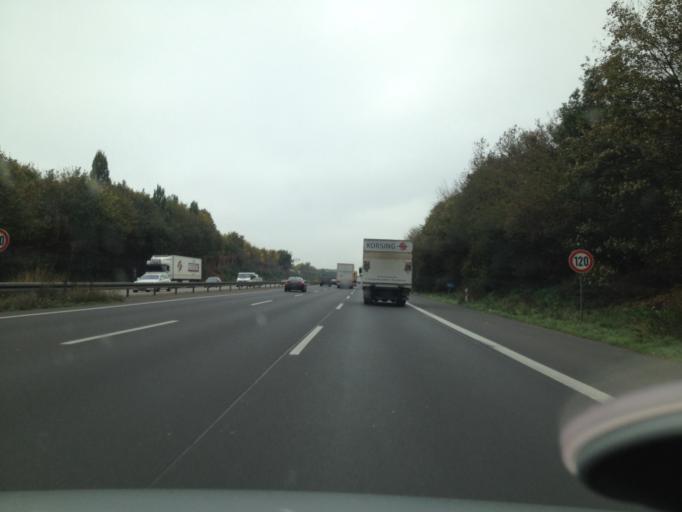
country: DE
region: North Rhine-Westphalia
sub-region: Regierungsbezirk Koln
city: Neustadt/Sued
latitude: 50.8992
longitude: 6.9080
